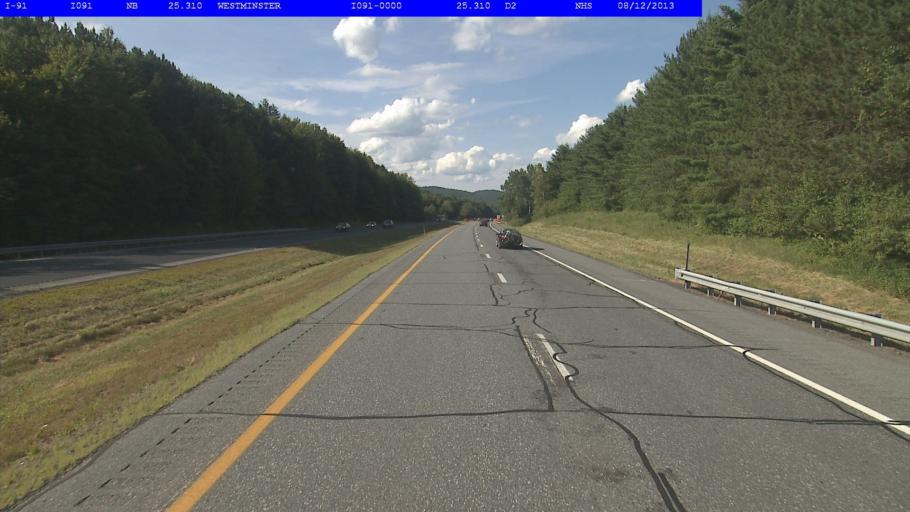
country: US
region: New Hampshire
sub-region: Cheshire County
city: Westmoreland
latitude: 43.0454
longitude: -72.4699
